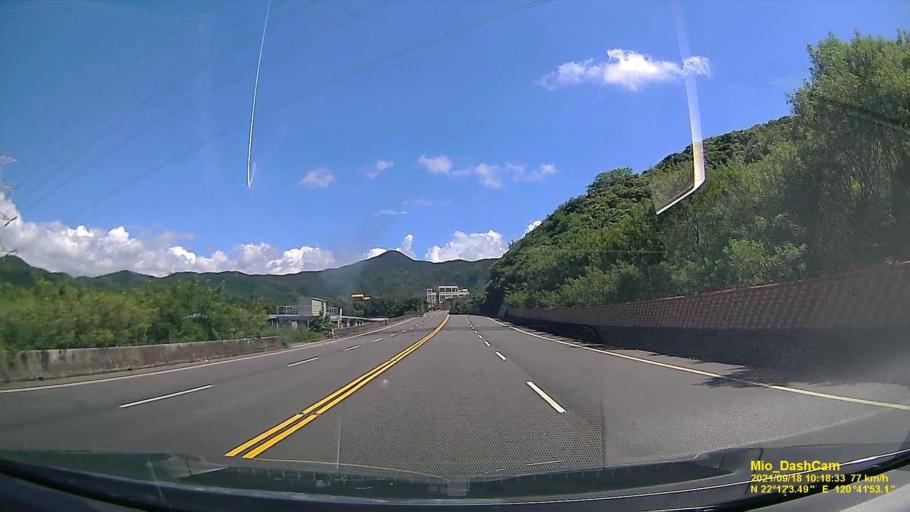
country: TW
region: Taiwan
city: Hengchun
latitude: 22.2010
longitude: 120.6980
